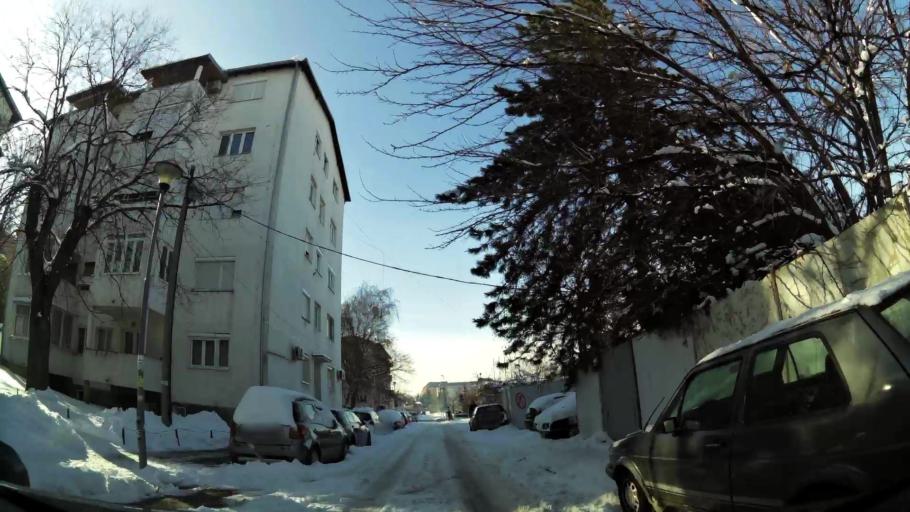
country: RS
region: Central Serbia
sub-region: Belgrade
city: Palilula
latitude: 44.8160
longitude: 20.5112
